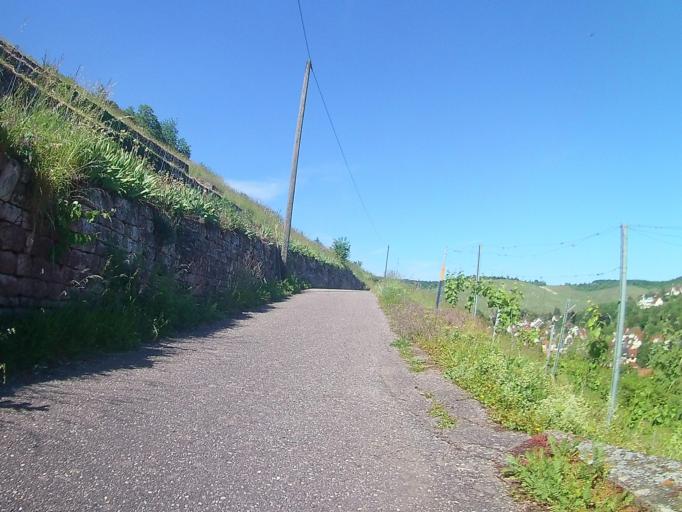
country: DE
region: Baden-Wuerttemberg
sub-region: Regierungsbezirk Stuttgart
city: Fellbach
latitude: 48.7706
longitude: 9.2708
